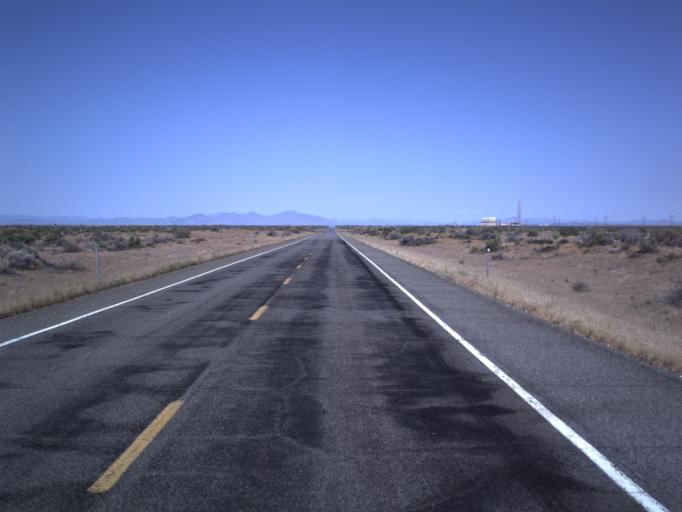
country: US
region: Utah
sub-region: Millard County
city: Delta
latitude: 39.4768
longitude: -112.4922
